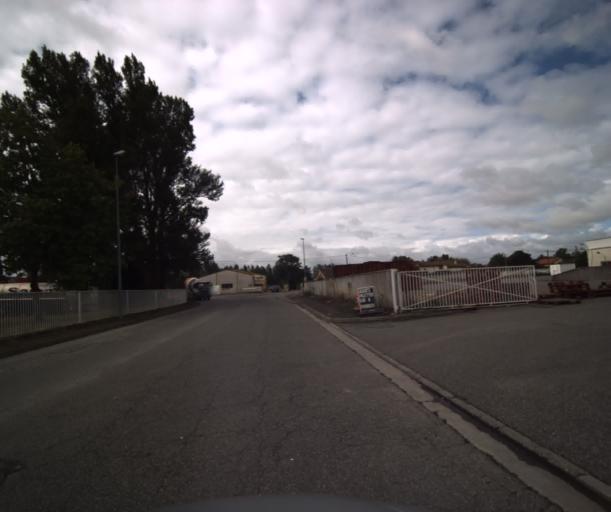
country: FR
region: Midi-Pyrenees
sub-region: Departement de la Haute-Garonne
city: Pinsaguel
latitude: 43.5280
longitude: 1.3787
